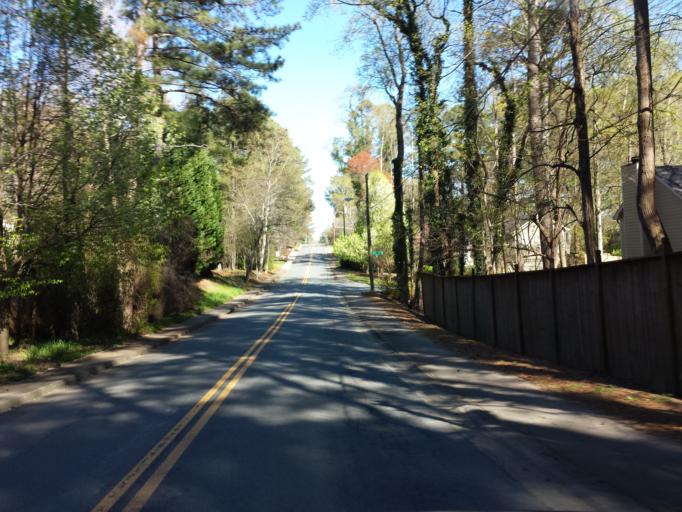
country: US
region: Georgia
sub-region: Cobb County
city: Marietta
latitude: 33.9595
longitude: -84.5713
